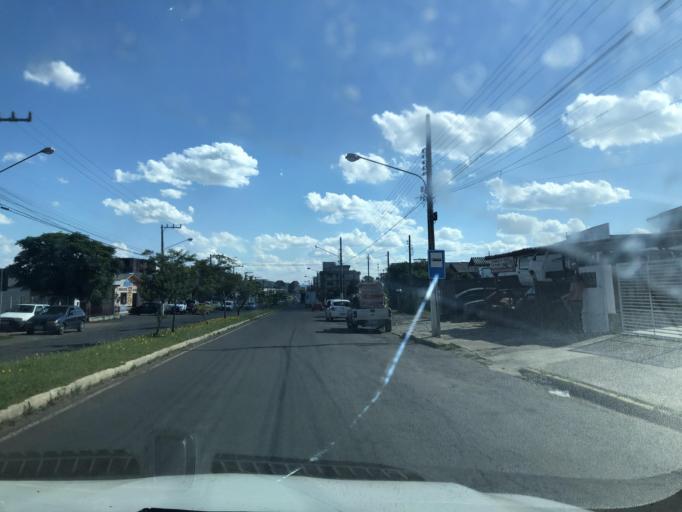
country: BR
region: Santa Catarina
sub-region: Lages
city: Lages
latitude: -27.8170
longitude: -50.3048
